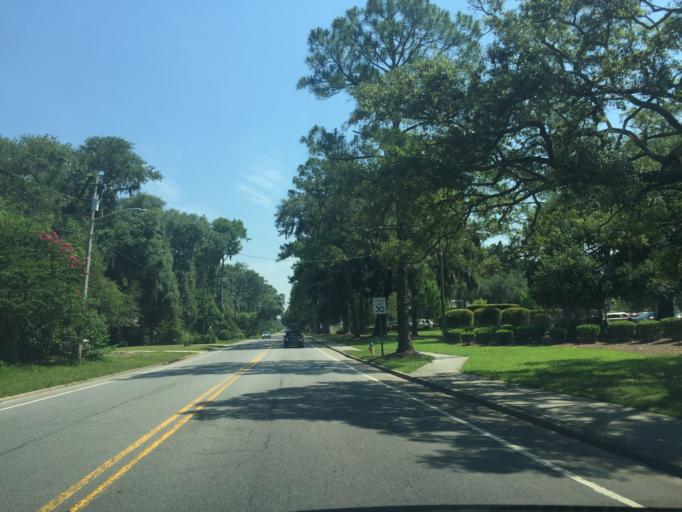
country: US
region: Georgia
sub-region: Chatham County
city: Savannah
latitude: 32.0284
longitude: -81.1057
